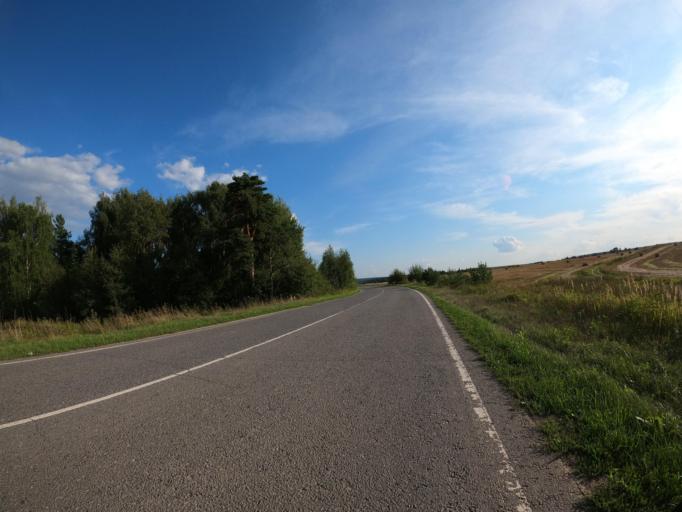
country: RU
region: Moskovskaya
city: Meshcherino
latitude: 55.1552
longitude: 38.4321
